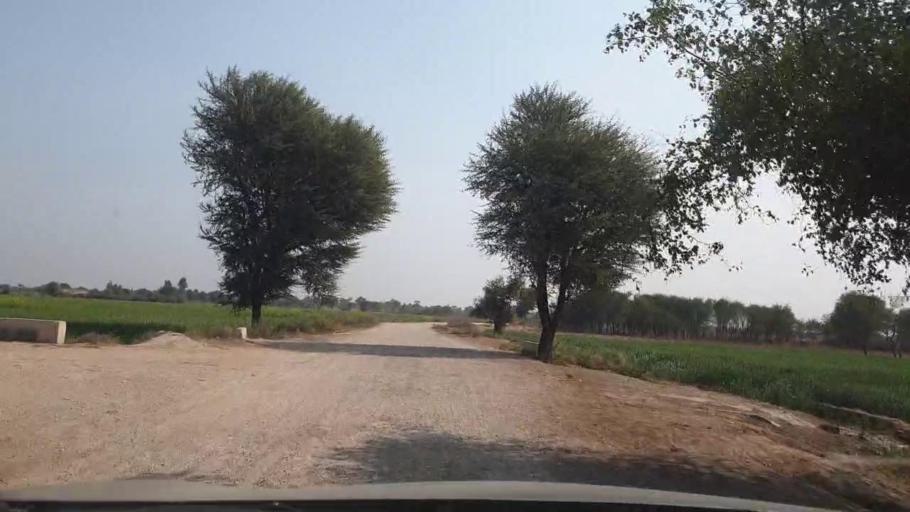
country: PK
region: Sindh
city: Tando Allahyar
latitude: 25.5620
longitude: 68.8254
